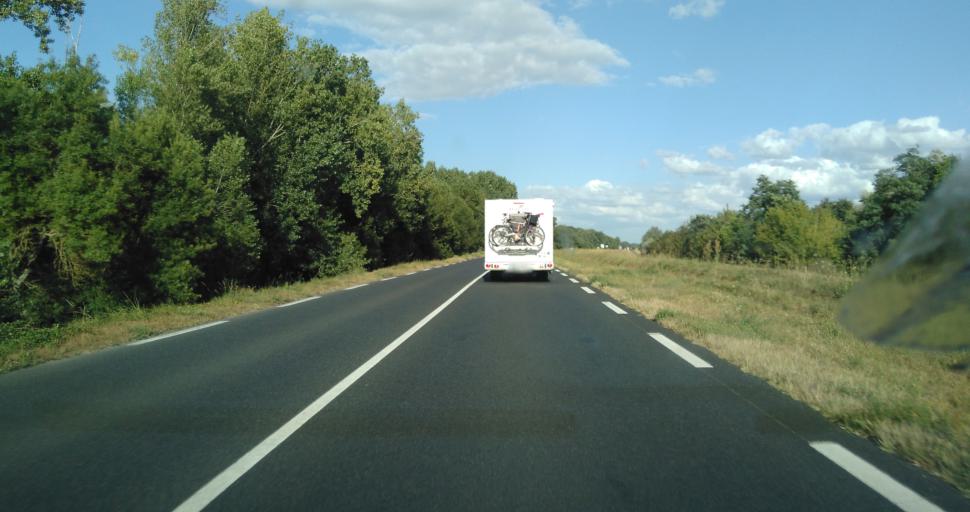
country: FR
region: Centre
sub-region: Departement d'Indre-et-Loire
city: Noizay
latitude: 47.4044
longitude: 0.8892
